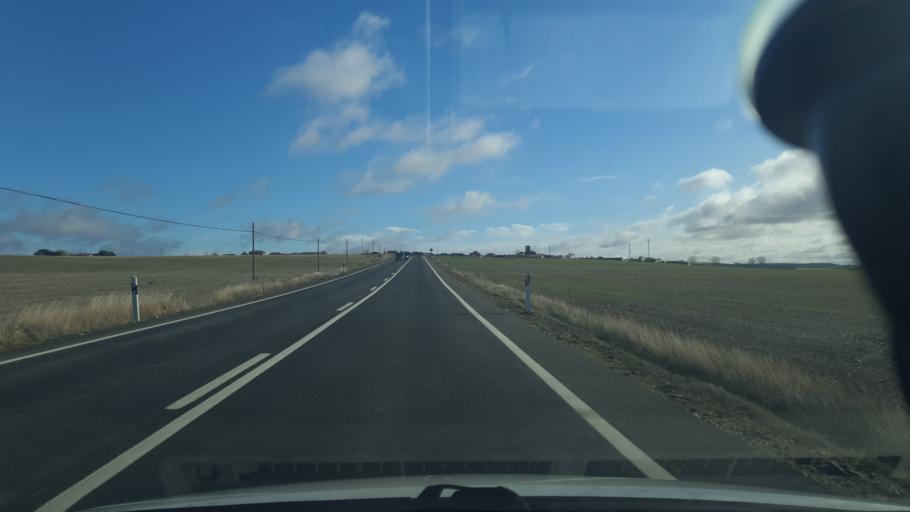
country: ES
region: Castille and Leon
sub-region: Provincia de Segovia
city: Codorniz
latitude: 41.0469
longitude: -4.6405
